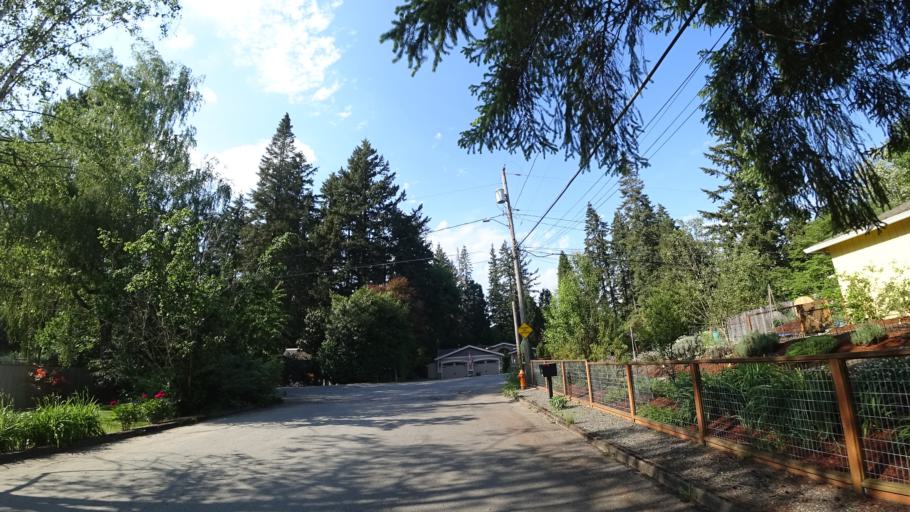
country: US
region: Oregon
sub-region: Washington County
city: Garden Home-Whitford
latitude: 45.4616
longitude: -122.7334
